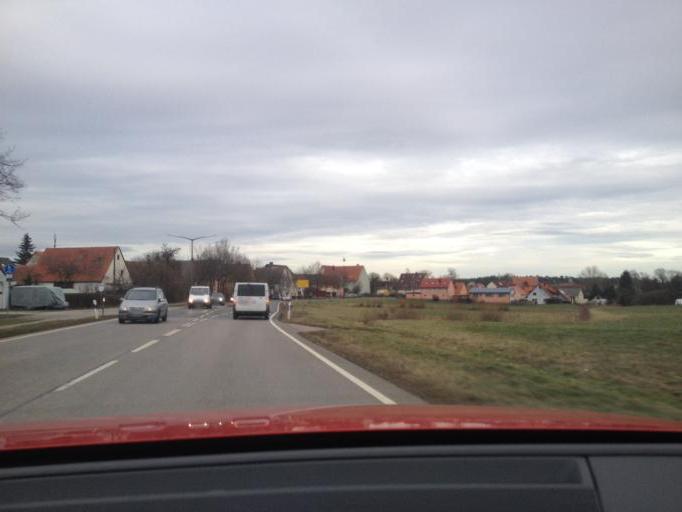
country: DE
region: Bavaria
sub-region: Regierungsbezirk Mittelfranken
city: Rosstal
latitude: 49.3809
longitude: 10.9298
